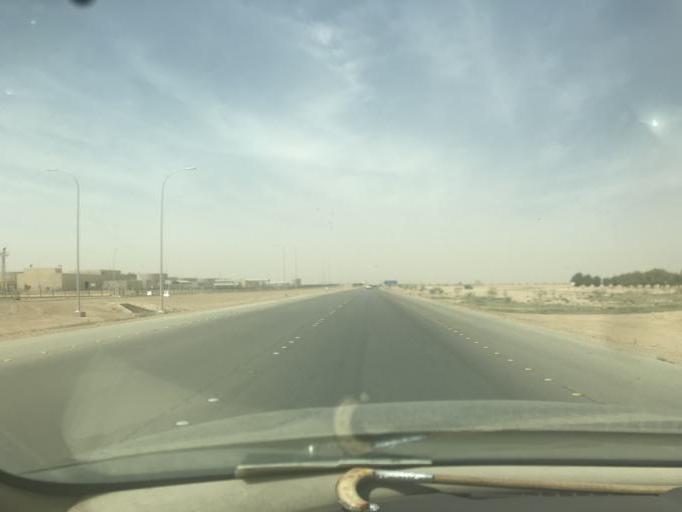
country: SA
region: Ar Riyad
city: Riyadh
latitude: 24.9787
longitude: 46.6857
